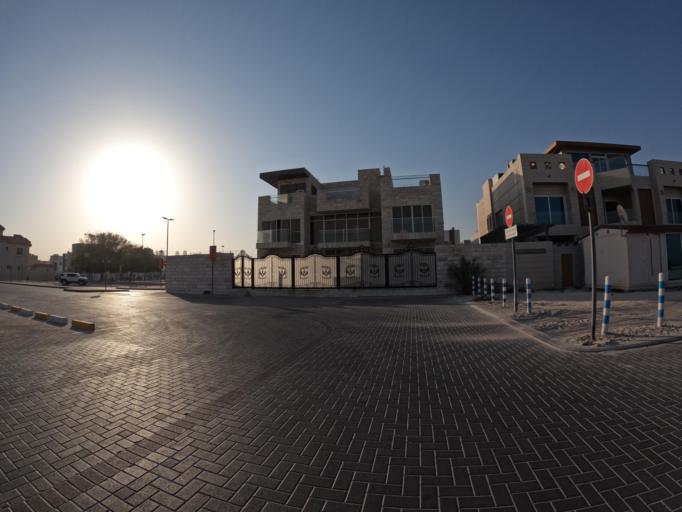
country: AE
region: Dubai
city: Dubai
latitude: 25.1783
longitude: 55.2199
